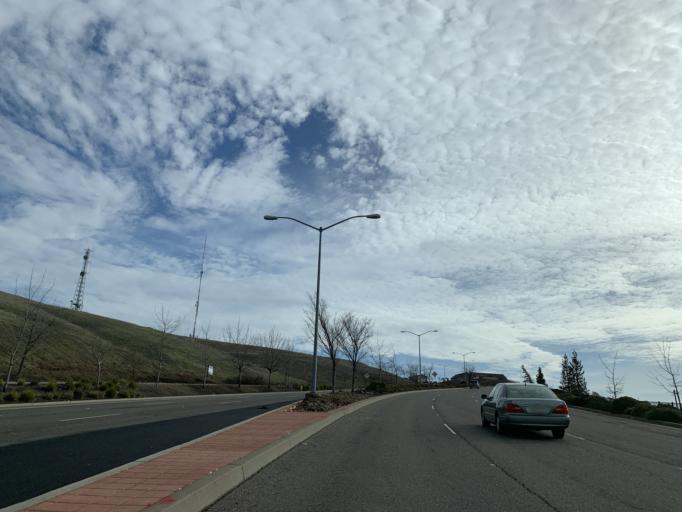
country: US
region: California
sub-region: El Dorado County
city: El Dorado Hills
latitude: 38.6478
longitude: -121.1033
